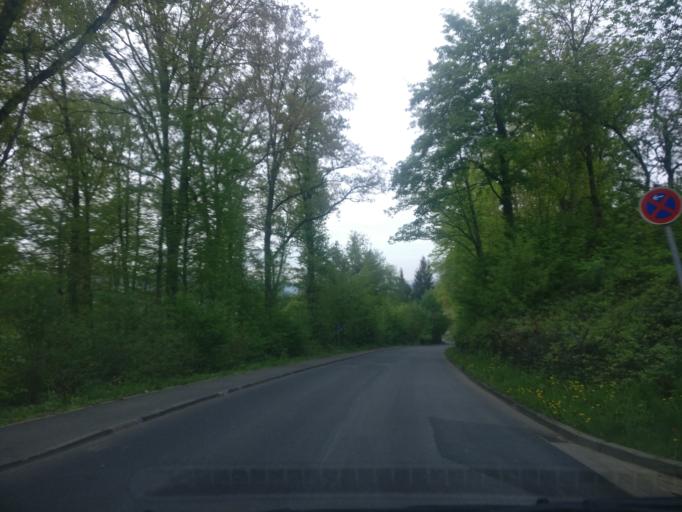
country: DE
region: Lower Saxony
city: Hannoversch Munden
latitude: 51.3982
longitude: 9.6568
